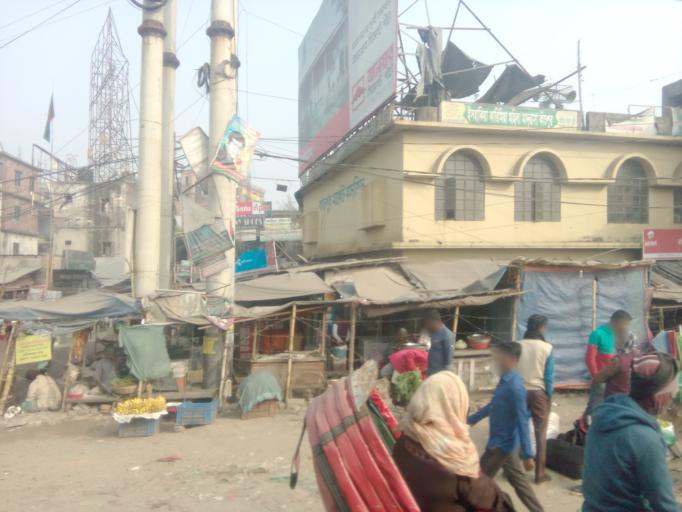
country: BD
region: Dhaka
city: Narayanganj
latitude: 23.7058
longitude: 90.5229
